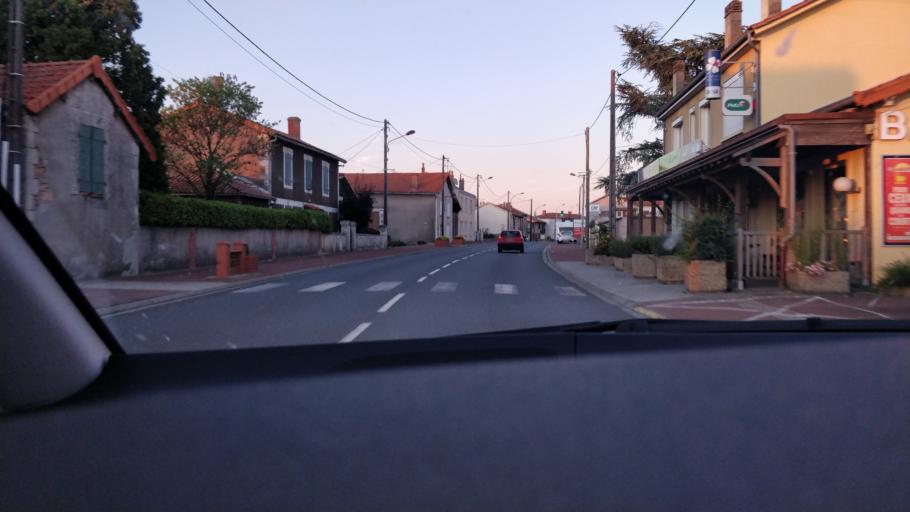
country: FR
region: Poitou-Charentes
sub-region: Departement de la Charente
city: Loubert
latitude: 45.8855
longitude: 0.5774
